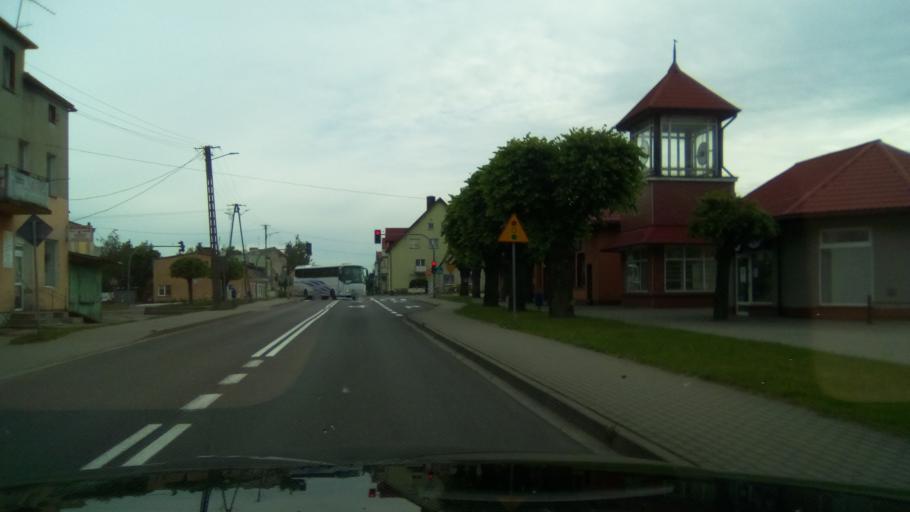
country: PL
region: Greater Poland Voivodeship
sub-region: Powiat wagrowiecki
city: Damaslawek
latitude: 52.8394
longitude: 17.4991
